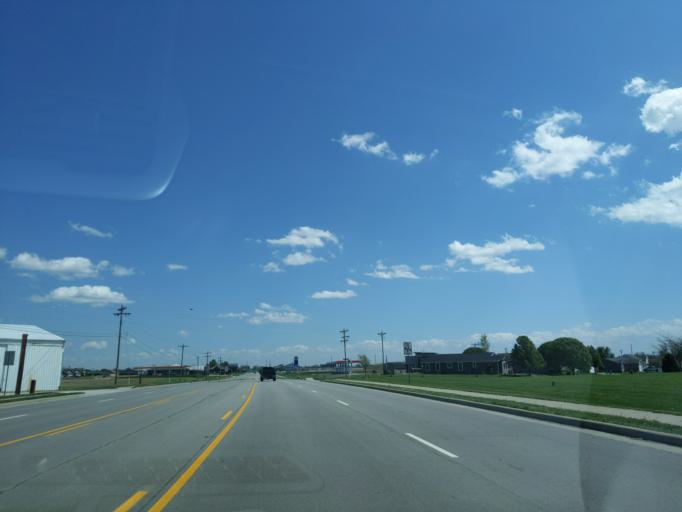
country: US
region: Indiana
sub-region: Decatur County
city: Greensburg
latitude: 39.3560
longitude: -85.5091
